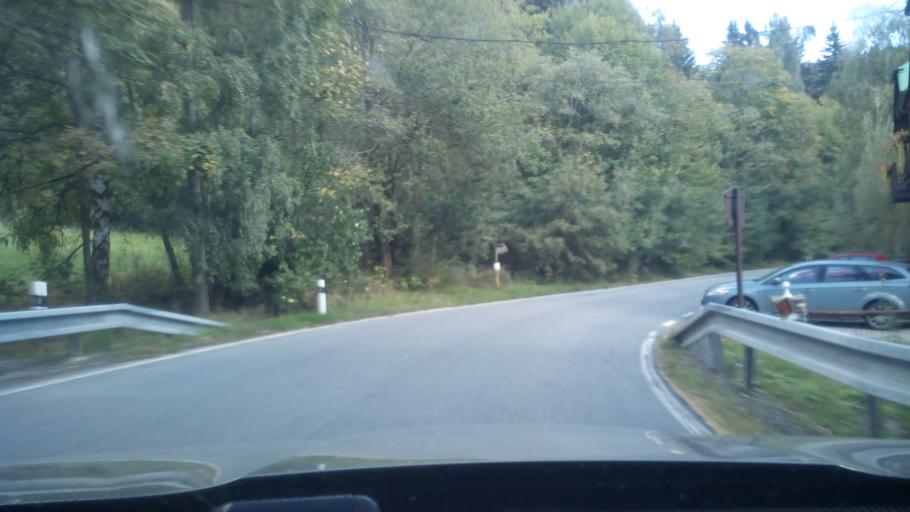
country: CZ
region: Plzensky
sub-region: Okres Klatovy
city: Kasperske Hory
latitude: 49.1437
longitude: 13.5965
